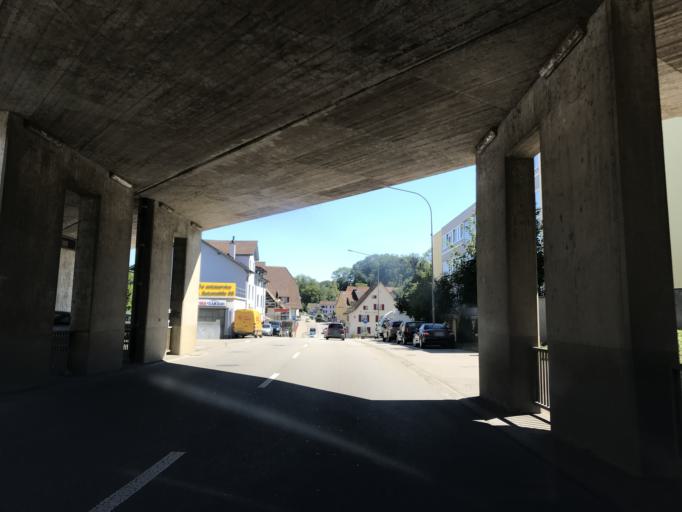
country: CH
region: Aargau
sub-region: Bezirk Rheinfelden
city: Kaiseraugst
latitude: 47.5353
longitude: 7.7168
